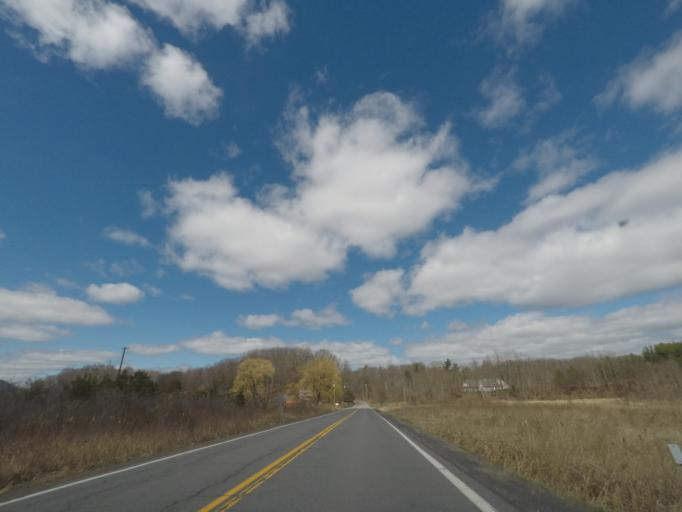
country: US
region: New York
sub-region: Albany County
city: Voorheesville
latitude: 42.6535
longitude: -73.9876
